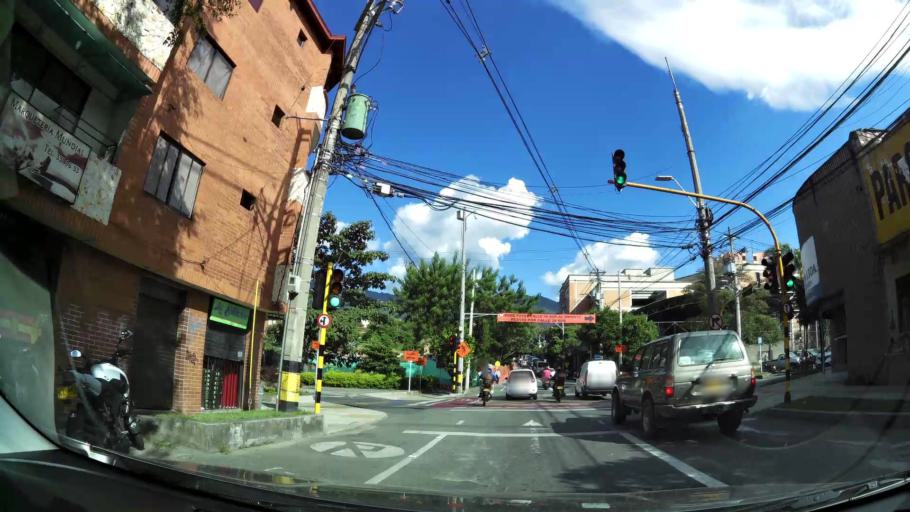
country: CO
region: Antioquia
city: Envigado
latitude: 6.1721
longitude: -75.5916
